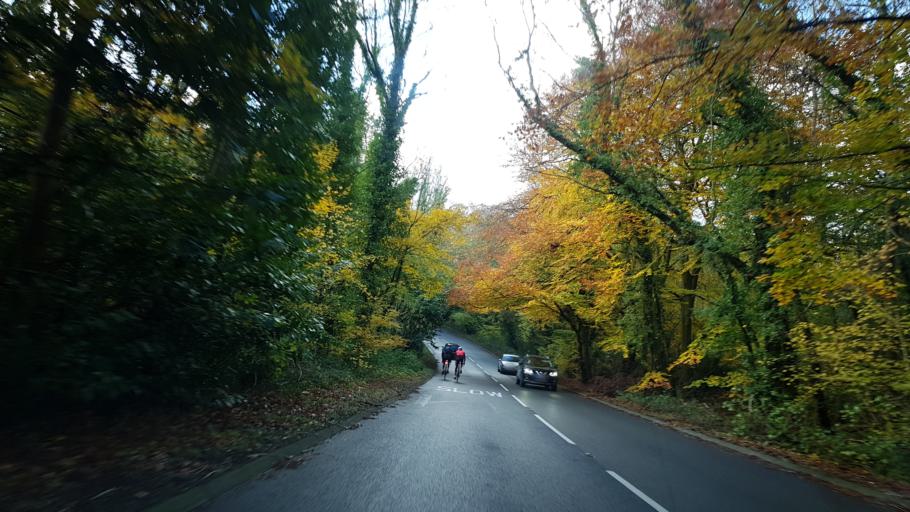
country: GB
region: England
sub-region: Surrey
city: Haslemere
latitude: 51.1072
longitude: -0.6886
